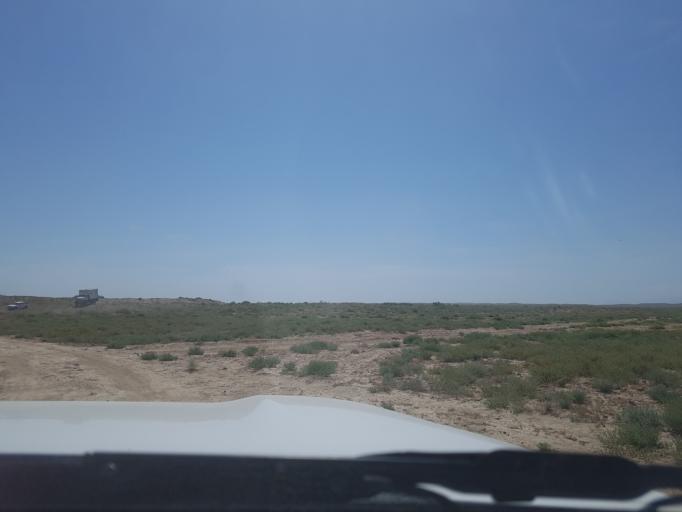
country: TM
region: Ahal
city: Baharly
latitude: 38.6063
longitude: 57.4333
